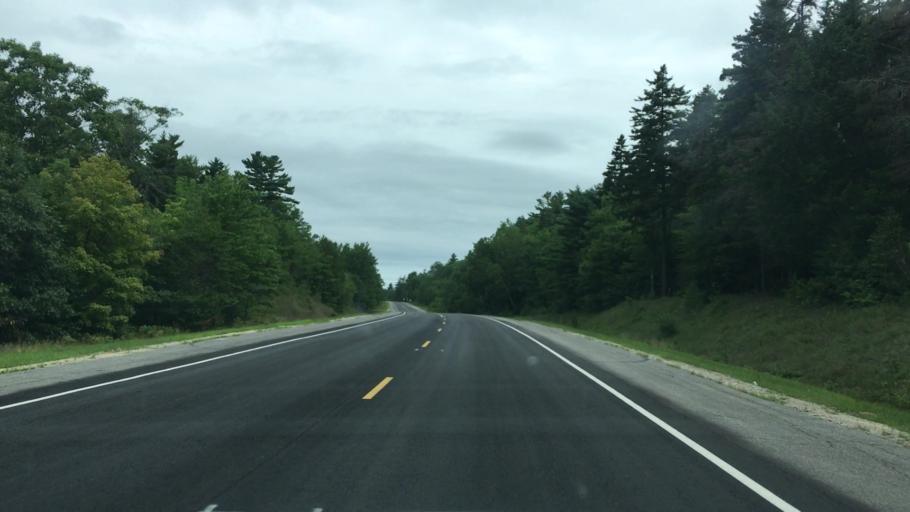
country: US
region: Maine
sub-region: Washington County
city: Cherryfield
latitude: 44.8983
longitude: -67.8556
